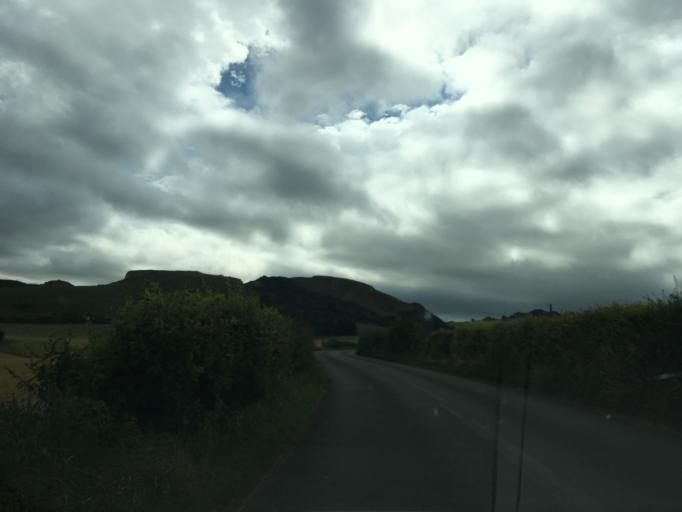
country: GB
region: Scotland
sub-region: East Lothian
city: Haddington
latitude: 55.9834
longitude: -2.7817
